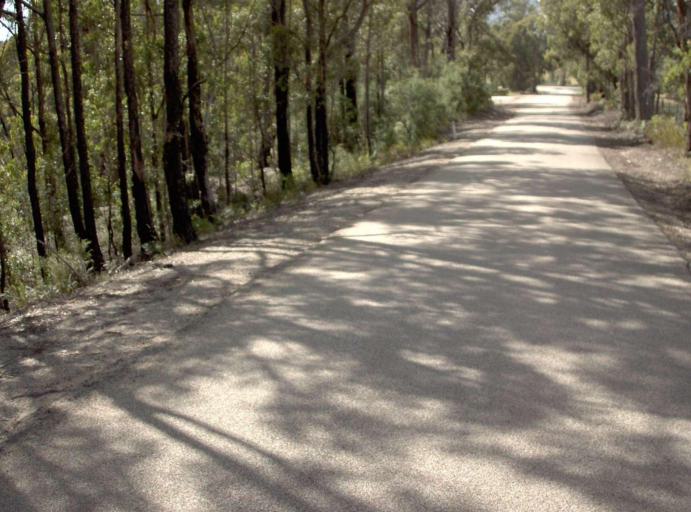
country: AU
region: Victoria
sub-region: East Gippsland
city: Lakes Entrance
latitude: -37.5255
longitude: 148.1546
